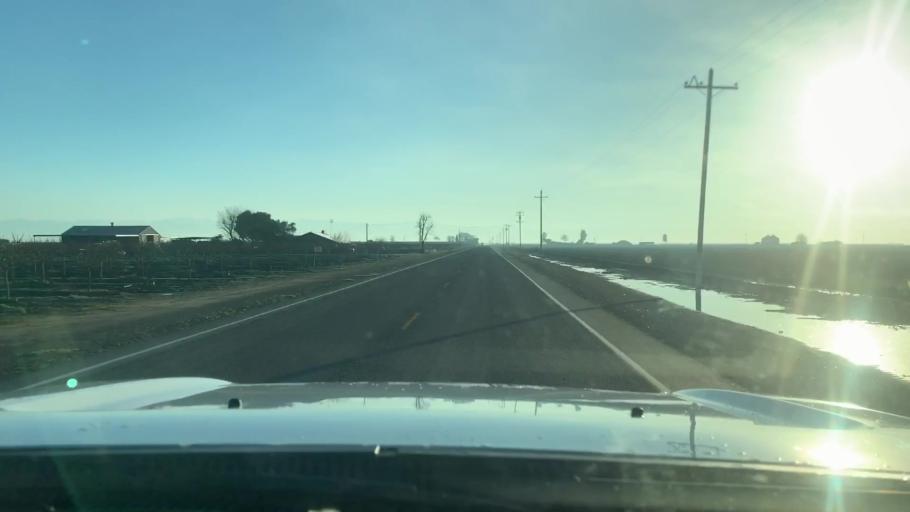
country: US
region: California
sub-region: Kings County
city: Home Garden
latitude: 36.2109
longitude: -119.5916
